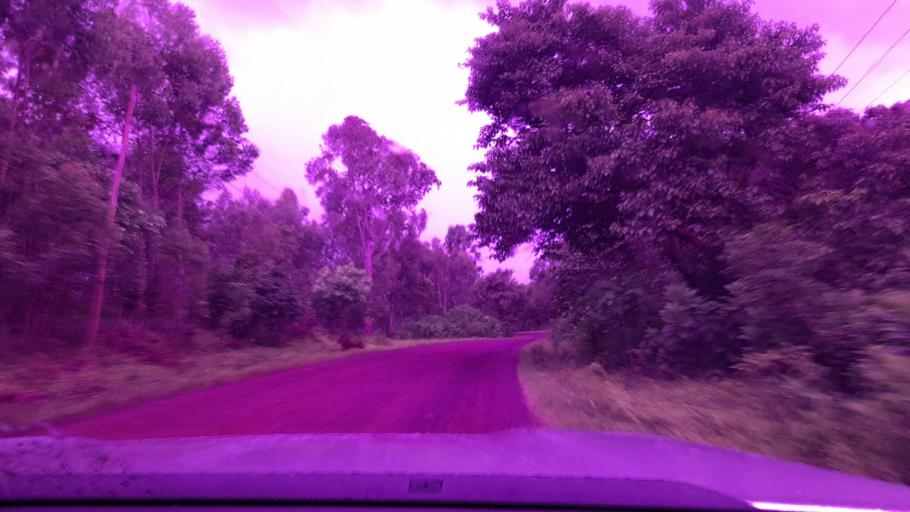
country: ET
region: Oromiya
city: Metu
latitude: 8.4458
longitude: 35.6263
